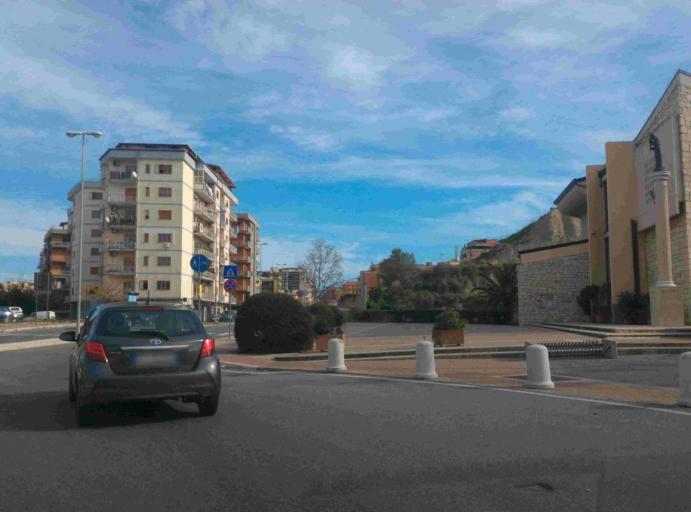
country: IT
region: Calabria
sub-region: Provincia di Crotone
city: Crotone
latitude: 39.0756
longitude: 17.1204
